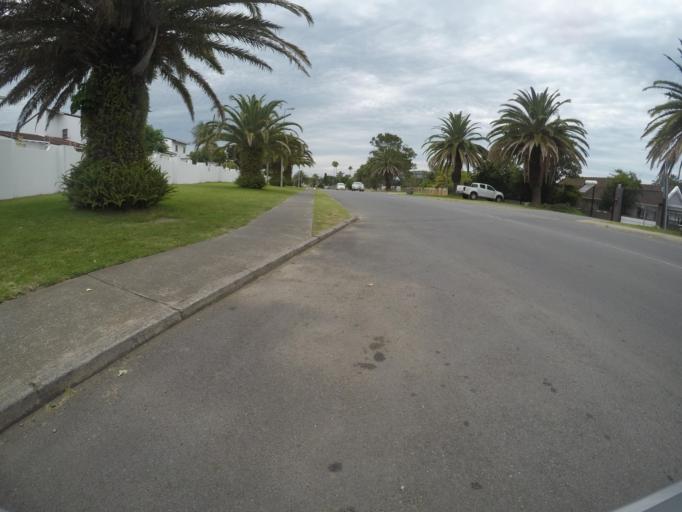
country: ZA
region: Eastern Cape
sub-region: Buffalo City Metropolitan Municipality
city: East London
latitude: -32.9755
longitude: 27.9409
